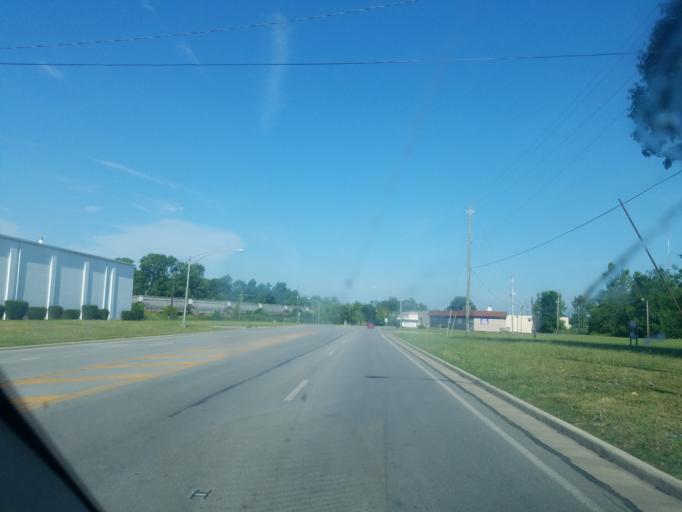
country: US
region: Ohio
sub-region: Allen County
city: Lima
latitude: 40.7532
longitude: -84.1285
